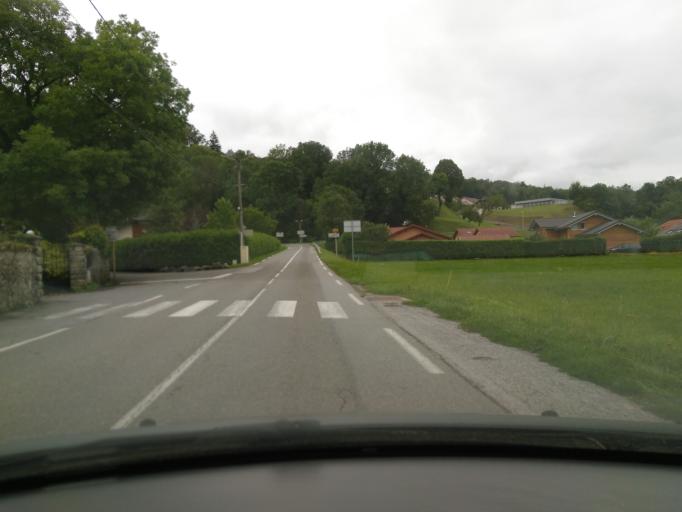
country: FR
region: Rhone-Alpes
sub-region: Departement de la Haute-Savoie
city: Bonneville
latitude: 46.0561
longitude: 6.3730
